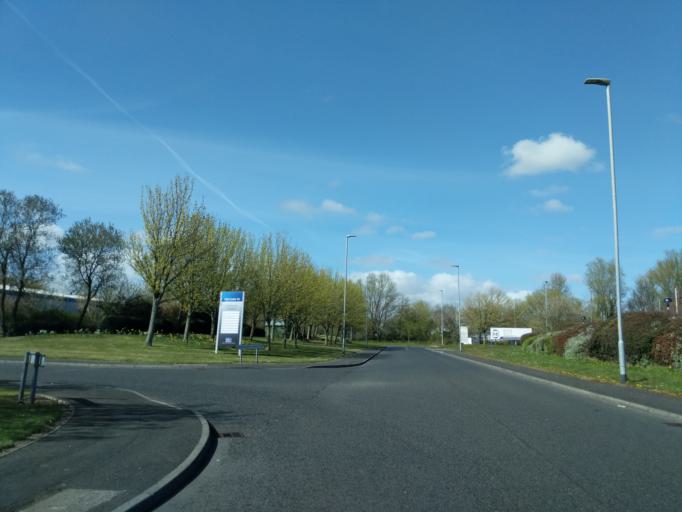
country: GB
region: England
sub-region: Northumberland
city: Cramlington
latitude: 55.0994
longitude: -1.6040
